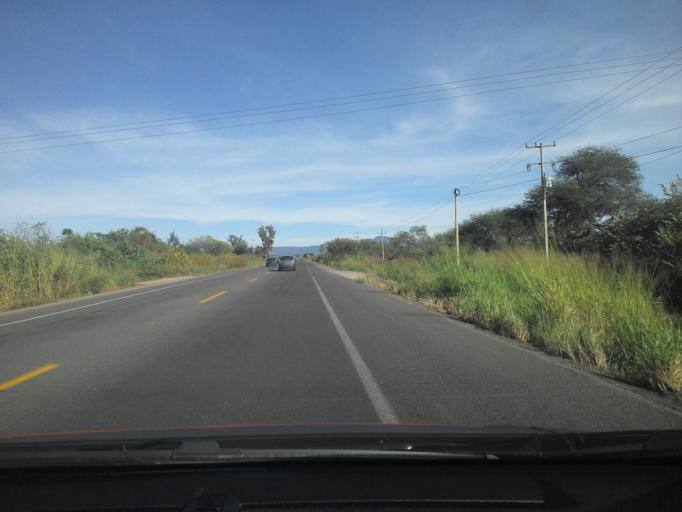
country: MX
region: Jalisco
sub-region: Teuchitlan
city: La Estanzuela
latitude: 20.6724
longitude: -103.8198
